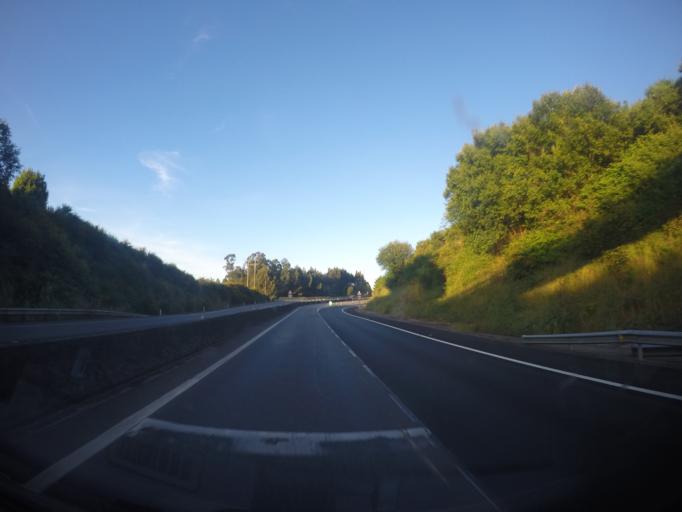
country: ES
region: Galicia
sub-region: Provincia da Coruna
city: Oroso
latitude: 42.9742
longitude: -8.4433
